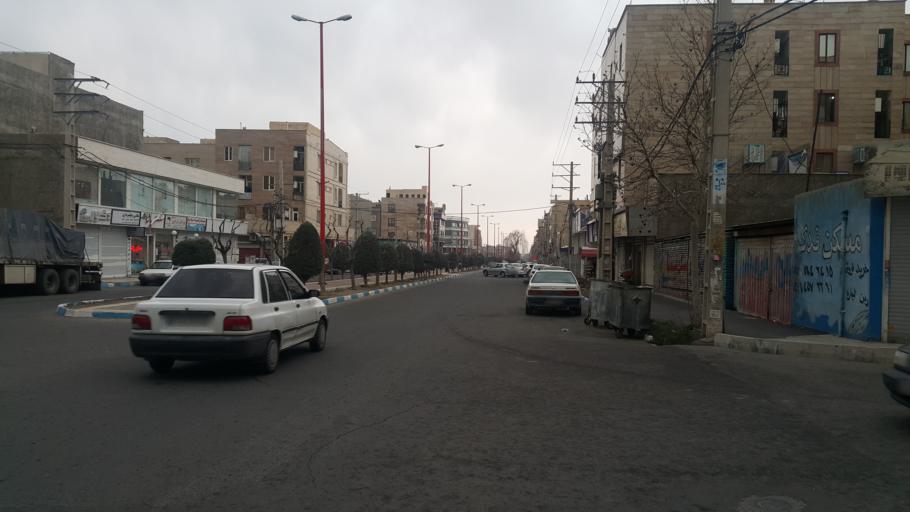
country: IR
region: Tehran
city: Shahre Jadide Andisheh
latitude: 35.6712
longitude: 51.0093
